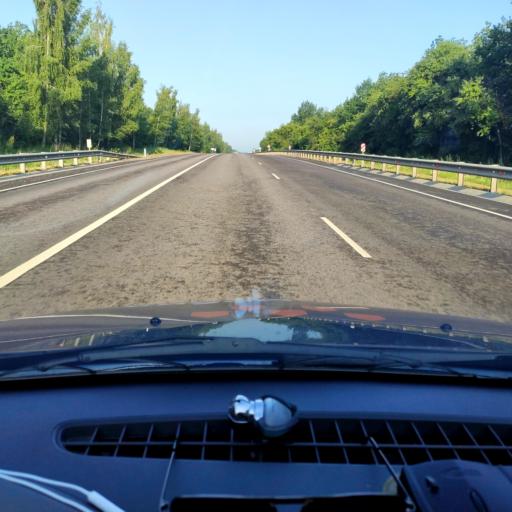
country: RU
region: Lipetsk
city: Izmalkovo
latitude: 52.4394
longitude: 37.9418
